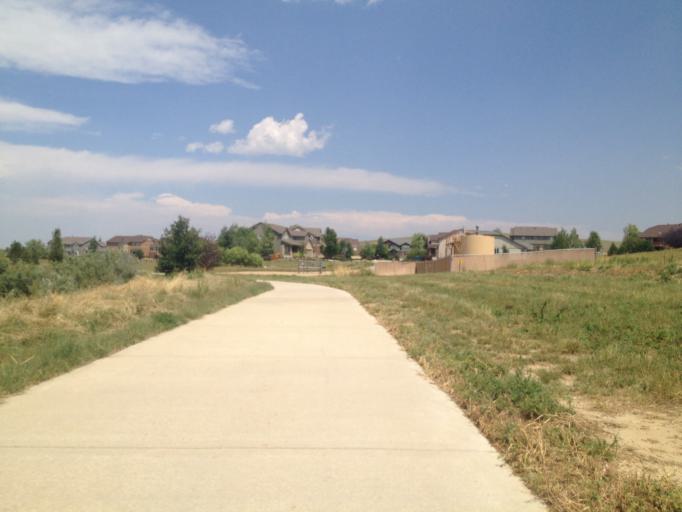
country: US
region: Colorado
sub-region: Boulder County
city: Erie
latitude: 40.0260
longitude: -105.0428
